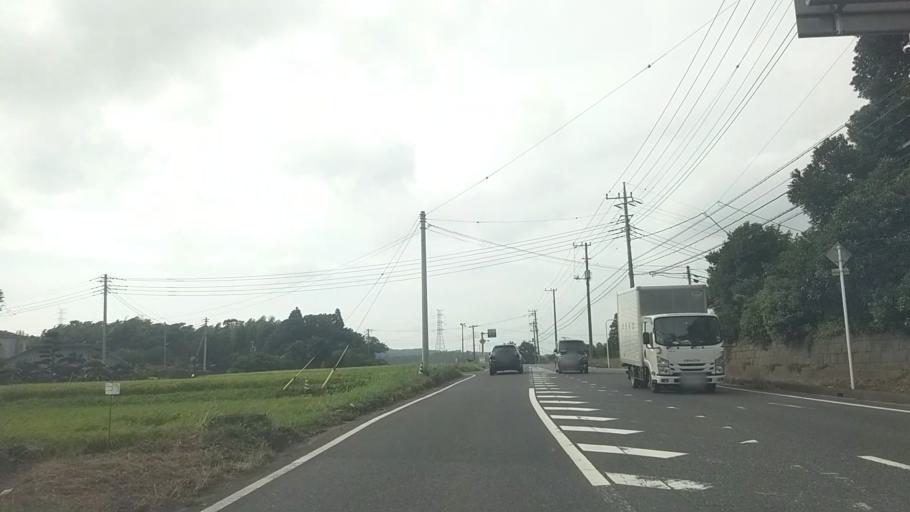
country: JP
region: Chiba
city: Kimitsu
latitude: 35.2779
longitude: 139.9915
